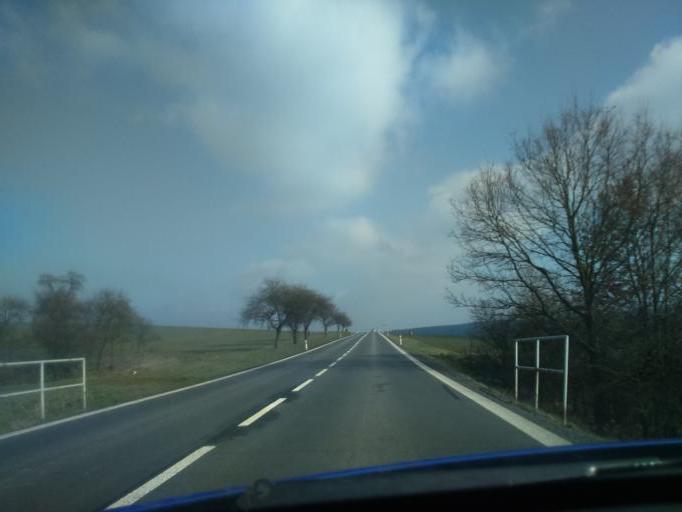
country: CZ
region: Plzensky
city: Blizejov
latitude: 49.5376
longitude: 12.9907
